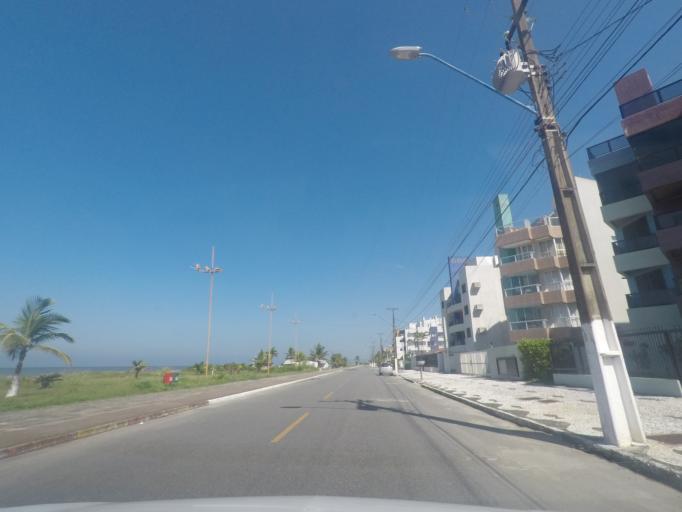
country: BR
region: Parana
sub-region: Pontal Do Parana
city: Pontal do Parana
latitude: -25.7245
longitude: -48.4849
